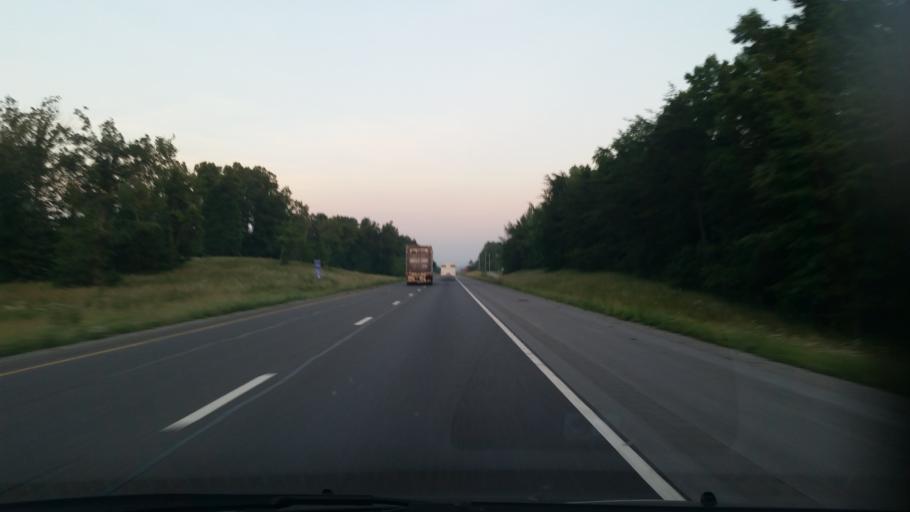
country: US
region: Tennessee
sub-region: Cumberland County
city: Crossville
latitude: 36.0265
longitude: -85.0879
